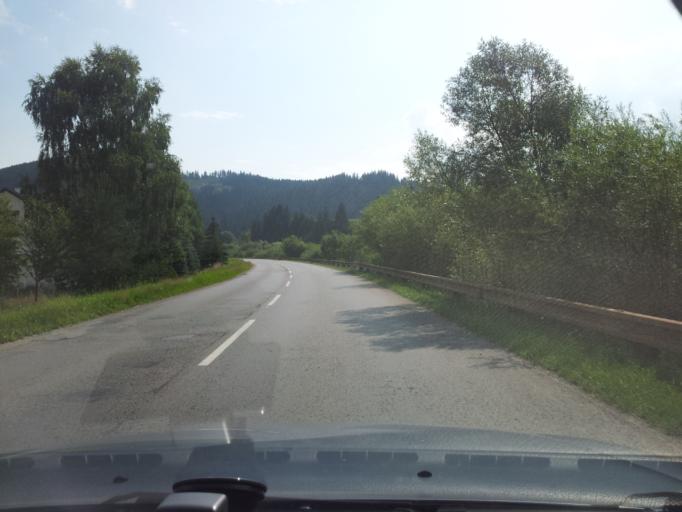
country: SK
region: Zilinsky
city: Namestovo
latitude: 49.3840
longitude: 19.3795
